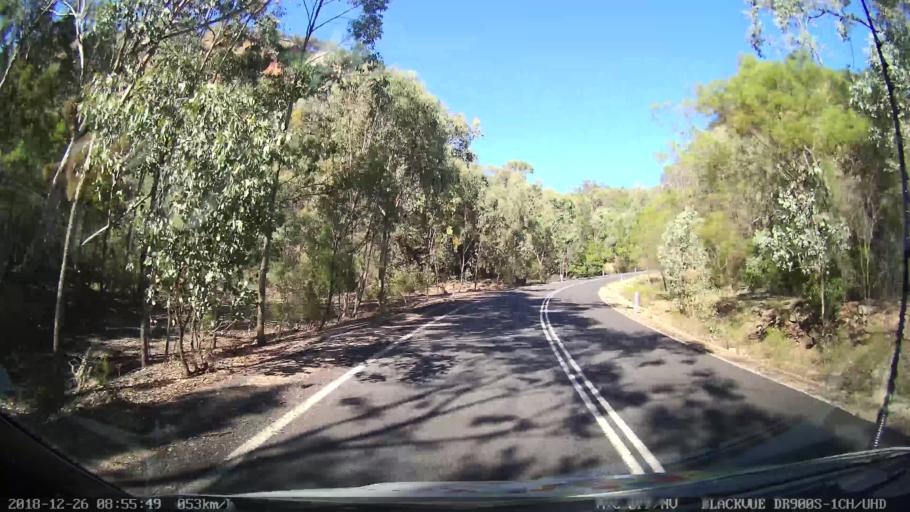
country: AU
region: New South Wales
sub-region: Mid-Western Regional
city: Kandos
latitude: -32.6209
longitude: 150.0616
